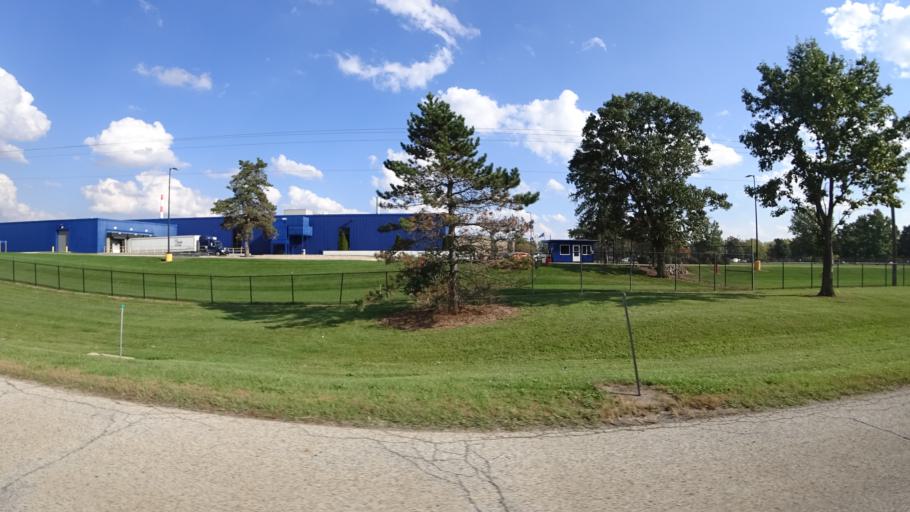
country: US
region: Michigan
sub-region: Saint Joseph County
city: Three Rivers
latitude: 41.9571
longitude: -85.6446
